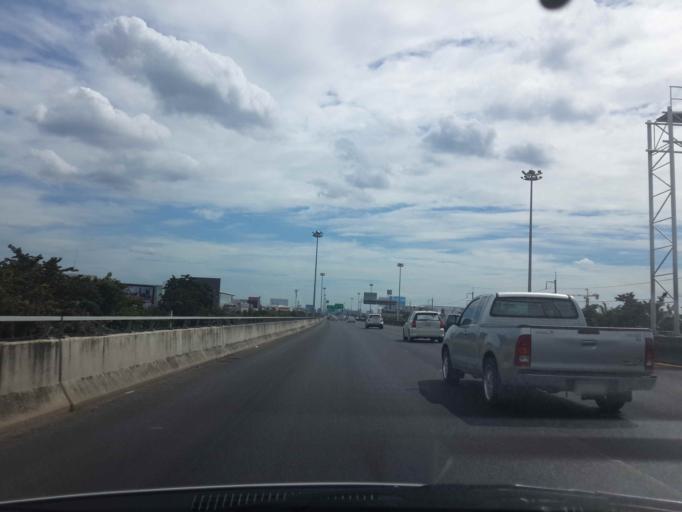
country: TH
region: Bangkok
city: Lat Phrao
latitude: 13.8086
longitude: 100.6188
